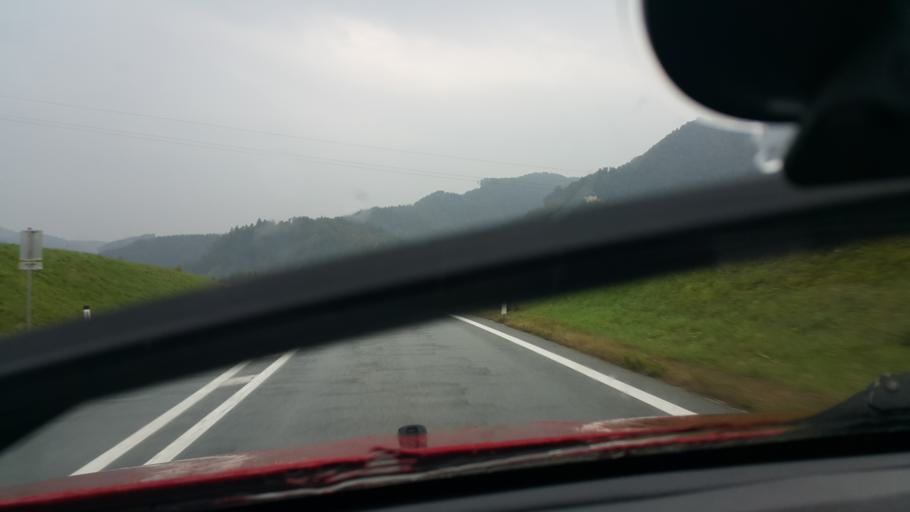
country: AT
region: Carinthia
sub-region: Politischer Bezirk Volkermarkt
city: Ruden
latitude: 46.6608
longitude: 14.7680
